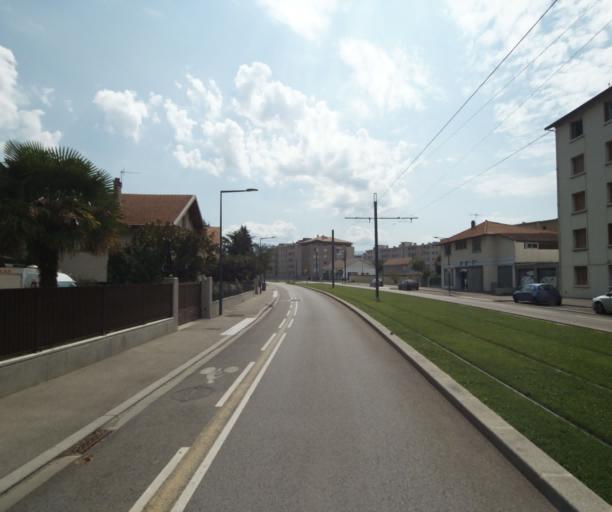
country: FR
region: Rhone-Alpes
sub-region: Departement de l'Isere
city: Fontaine
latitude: 45.2156
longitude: 5.6955
